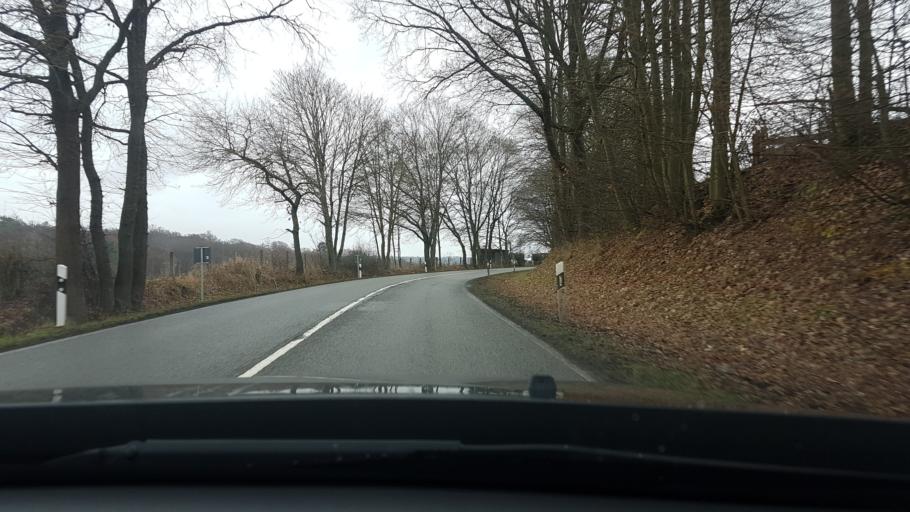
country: DE
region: Hesse
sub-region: Regierungsbezirk Kassel
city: Bad Arolsen
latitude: 51.4993
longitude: 9.0039
